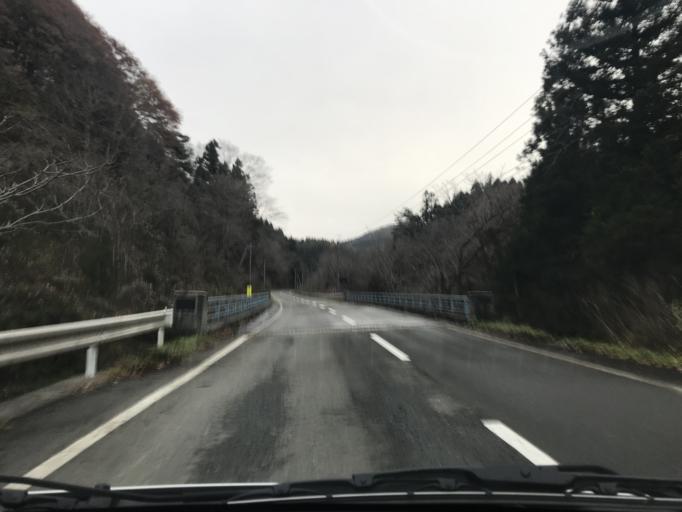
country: JP
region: Iwate
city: Tono
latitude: 39.1825
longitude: 141.3593
